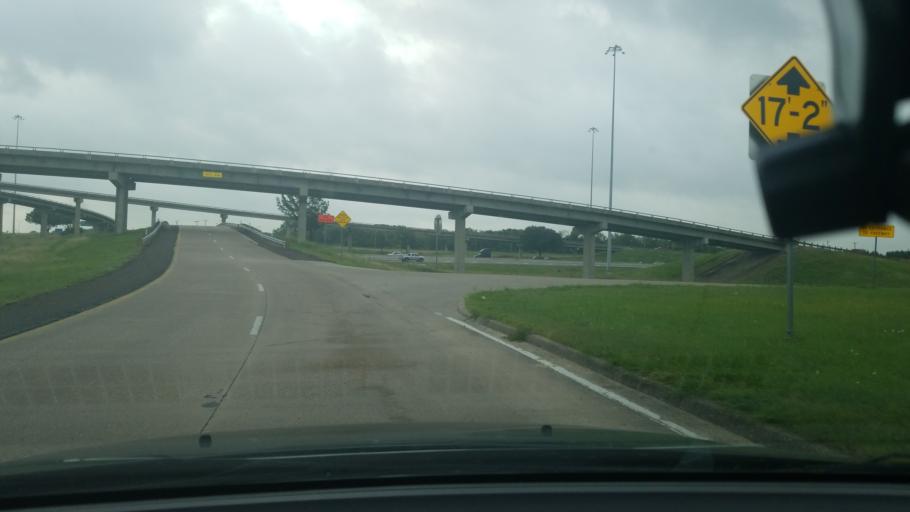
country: US
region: Texas
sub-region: Dallas County
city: Mesquite
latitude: 32.7912
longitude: -96.6269
